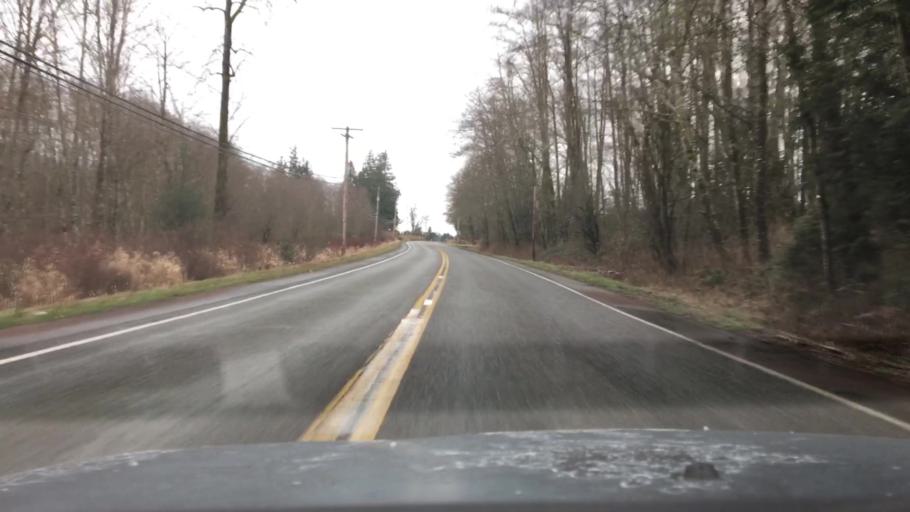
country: US
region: Washington
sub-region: Whatcom County
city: Sudden Valley
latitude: 48.6549
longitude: -122.3247
